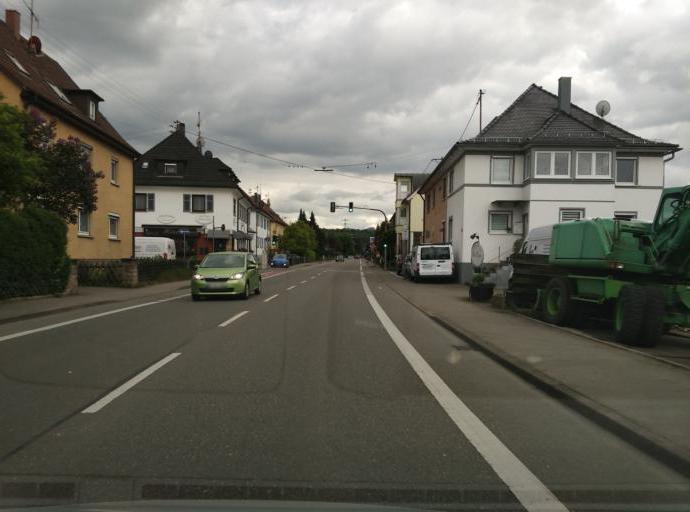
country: DE
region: Baden-Wuerttemberg
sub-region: Regierungsbezirk Stuttgart
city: Nurtingen
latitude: 48.6193
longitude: 9.3442
